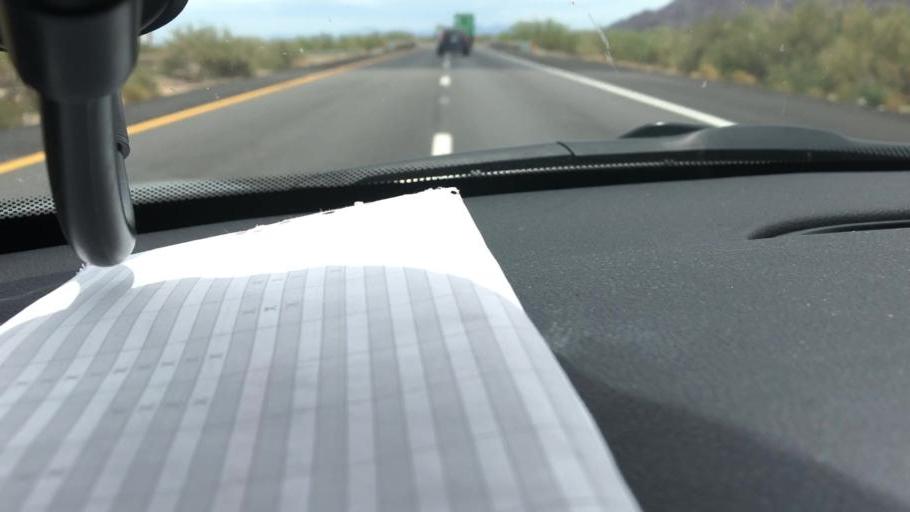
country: US
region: California
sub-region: Imperial County
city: Niland
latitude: 33.6812
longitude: -115.5465
